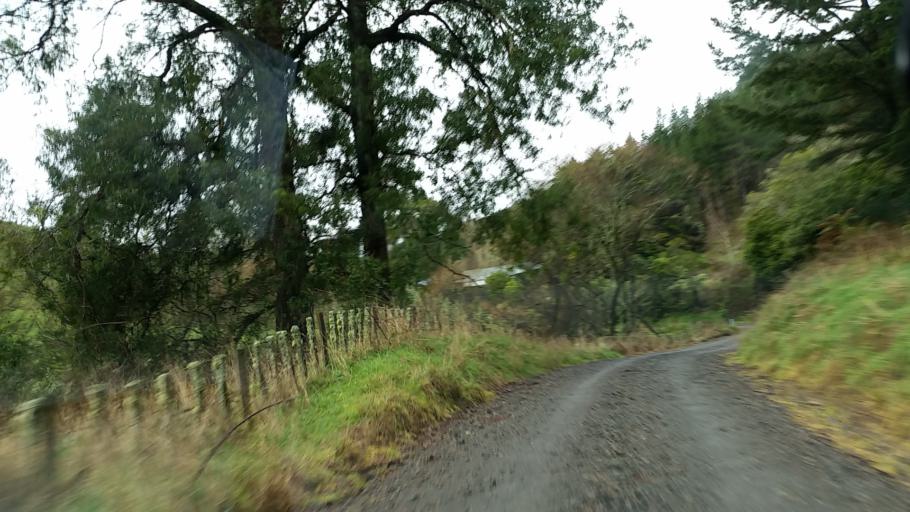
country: NZ
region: Taranaki
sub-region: South Taranaki District
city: Eltham
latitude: -39.5020
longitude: 174.4171
